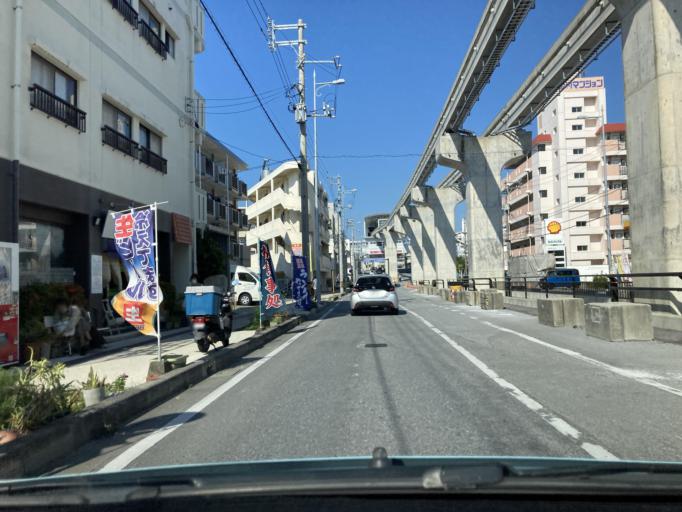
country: JP
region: Okinawa
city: Naha-shi
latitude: 26.2250
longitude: 127.7281
